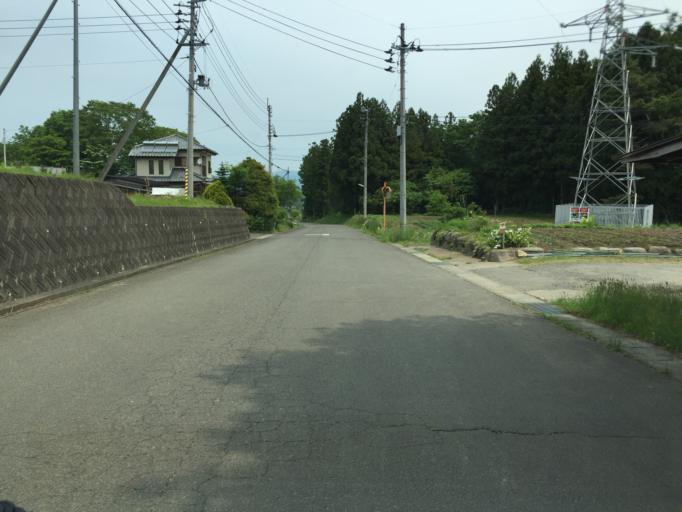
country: JP
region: Fukushima
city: Fukushima-shi
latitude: 37.7056
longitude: 140.3475
